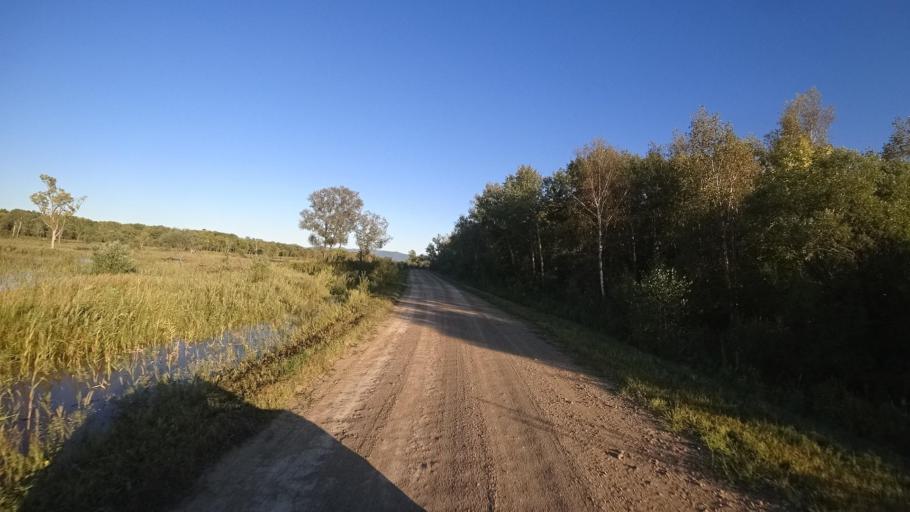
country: RU
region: Primorskiy
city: Kirovskiy
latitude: 44.8205
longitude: 133.6058
